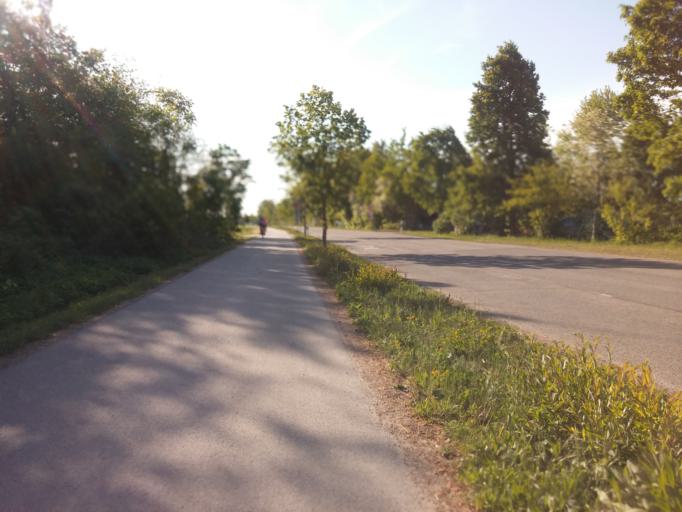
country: DE
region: Bavaria
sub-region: Upper Bavaria
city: Vaterstetten
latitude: 48.1226
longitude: 11.7531
